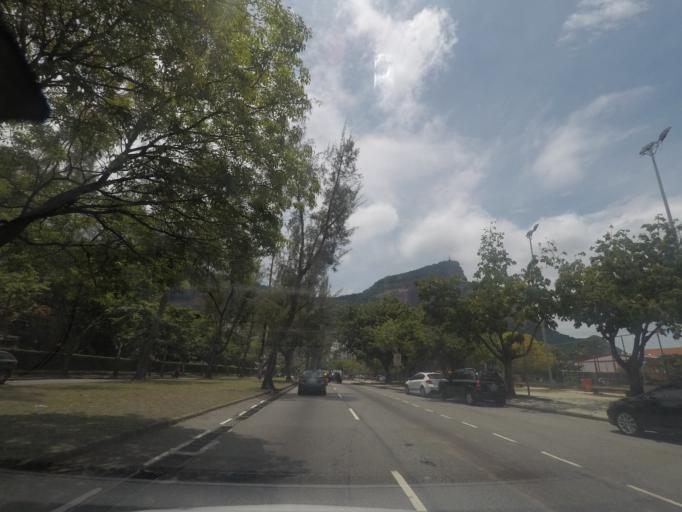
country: BR
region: Rio de Janeiro
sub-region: Rio De Janeiro
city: Rio de Janeiro
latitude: -22.9700
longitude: -43.2174
